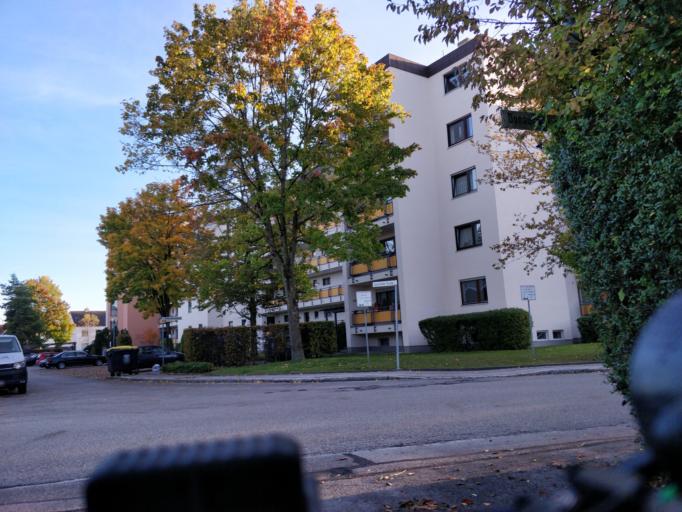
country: DE
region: Bavaria
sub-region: Swabia
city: Mering
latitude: 48.2796
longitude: 10.9712
